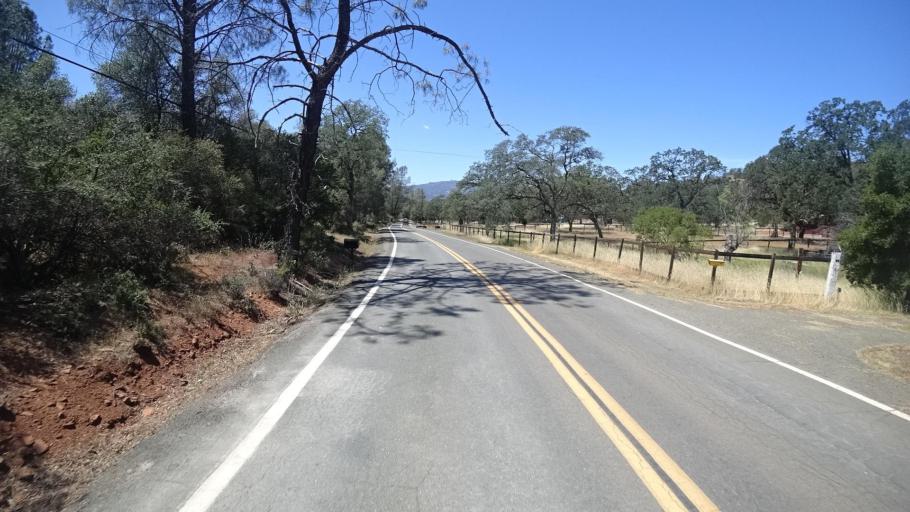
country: US
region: California
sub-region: Lake County
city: Hidden Valley Lake
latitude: 38.8221
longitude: -122.5542
